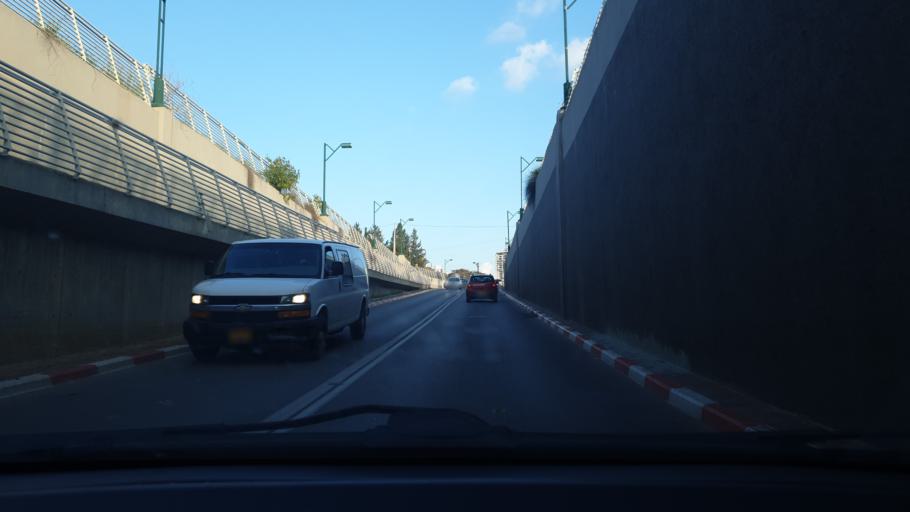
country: IL
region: Central District
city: Ramla
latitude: 31.9357
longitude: 34.8390
